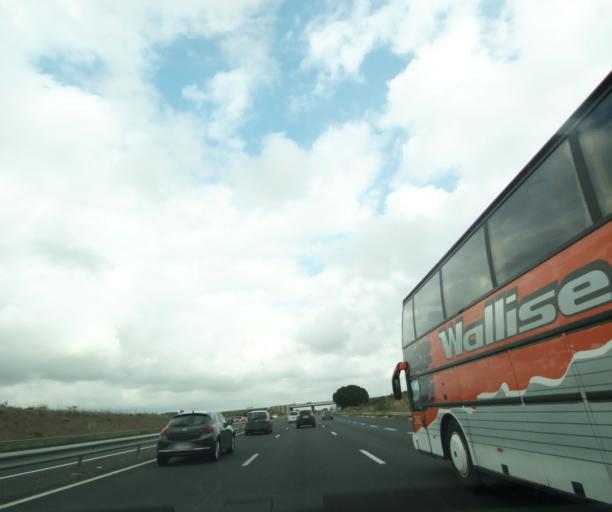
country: FR
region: Languedoc-Roussillon
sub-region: Departement de l'Herault
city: Cers
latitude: 43.3379
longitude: 3.2924
